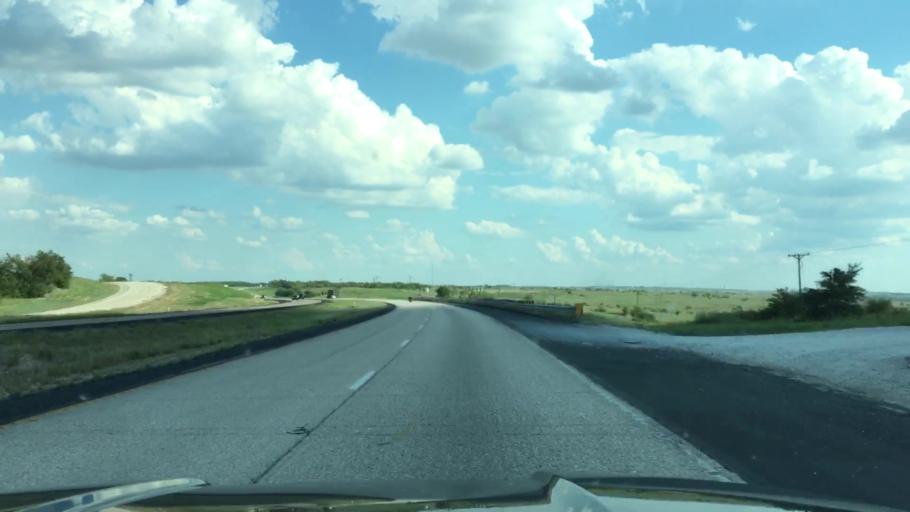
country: US
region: Texas
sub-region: Wise County
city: New Fairview
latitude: 33.1278
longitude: -97.4912
